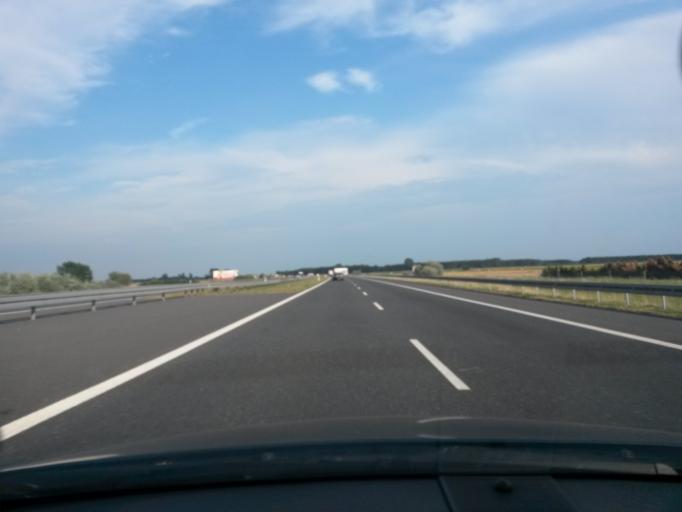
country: PL
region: Lodz Voivodeship
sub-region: Powiat poddebicki
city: Dalikow
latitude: 51.9594
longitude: 19.1260
